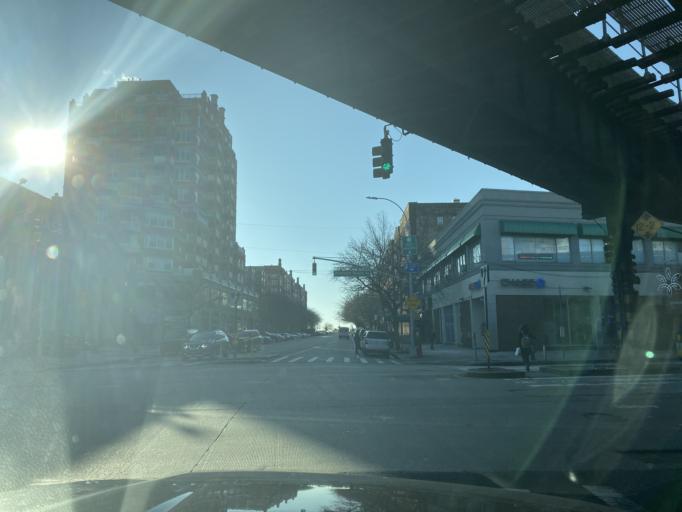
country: US
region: New York
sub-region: Kings County
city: Coney Island
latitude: 40.5782
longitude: -73.9597
